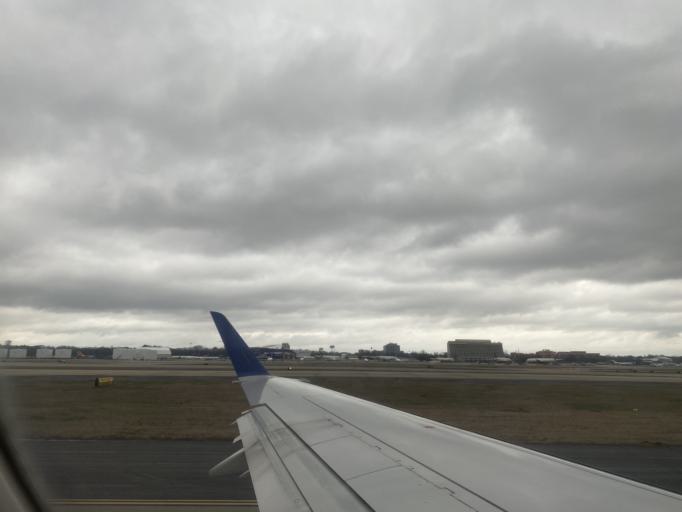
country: US
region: Georgia
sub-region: Fulton County
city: College Park
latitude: 33.6446
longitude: -84.4300
